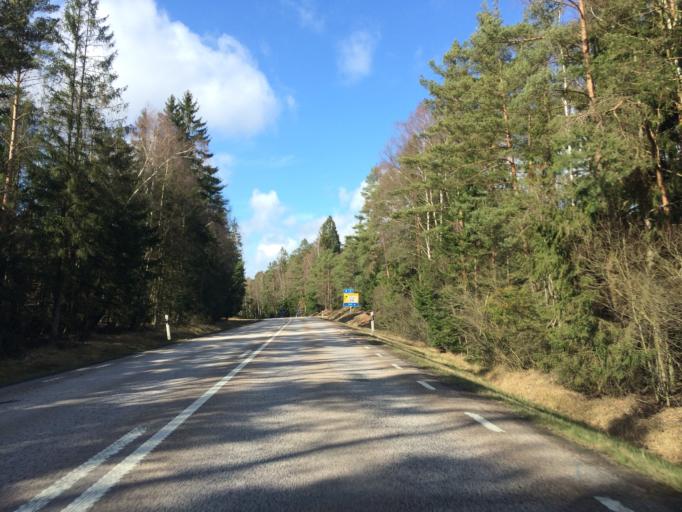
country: SE
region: Kronoberg
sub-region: Markaryds Kommun
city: Markaryd
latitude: 56.4902
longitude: 13.4708
